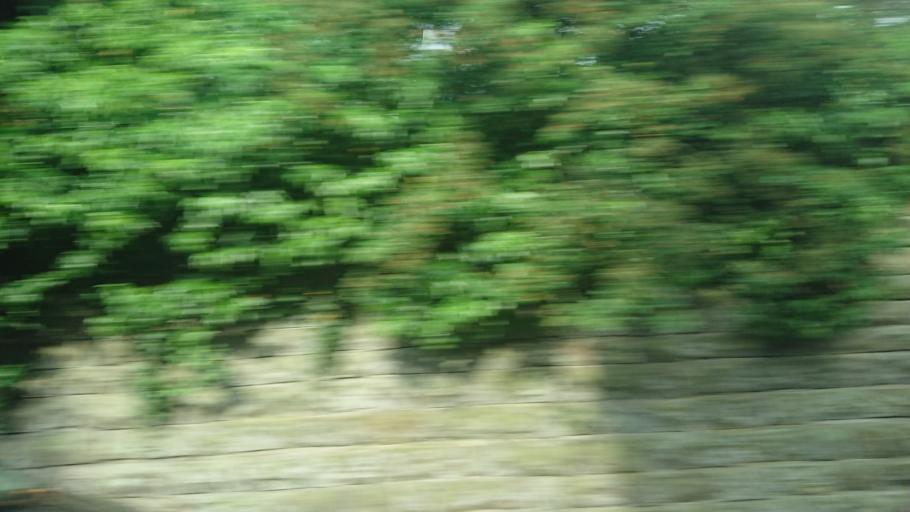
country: GB
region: England
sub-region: North Yorkshire
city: High Bentham
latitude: 54.1167
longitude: -2.5100
